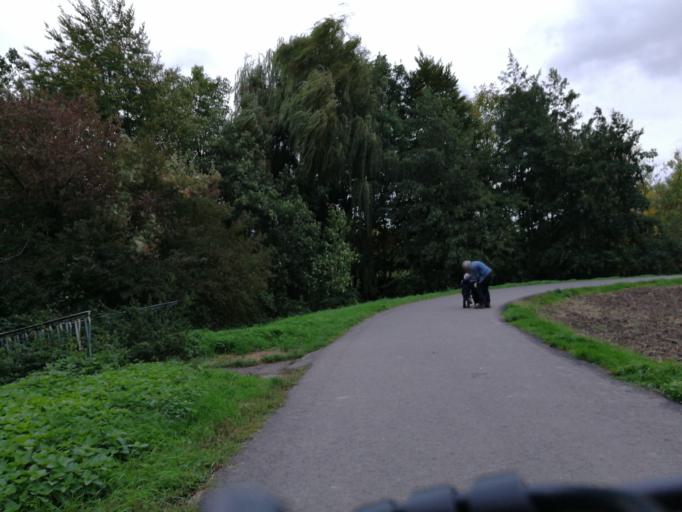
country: DE
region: North Rhine-Westphalia
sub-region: Regierungsbezirk Dusseldorf
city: Neuss
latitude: 51.1410
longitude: 6.7412
